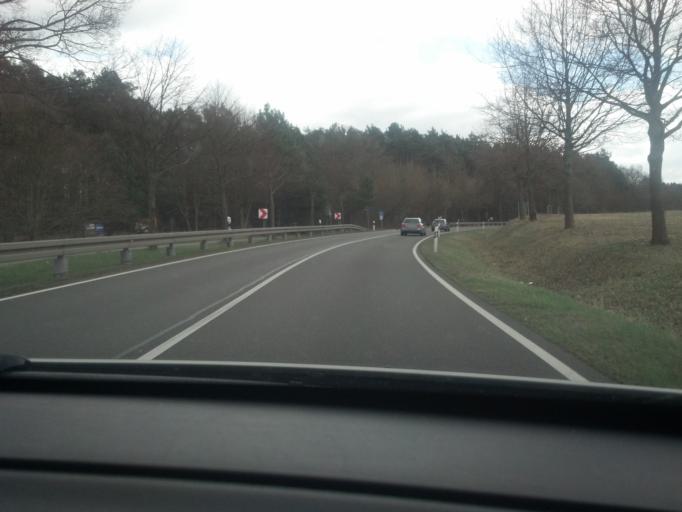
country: DE
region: Mecklenburg-Vorpommern
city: Rechlin
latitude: 53.2898
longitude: 12.7922
